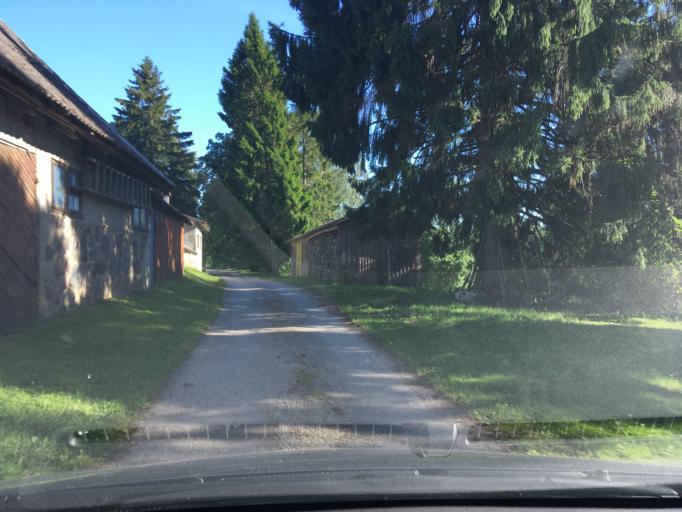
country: EE
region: Laeaene
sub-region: Lihula vald
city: Lihula
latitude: 58.5827
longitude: 23.7365
